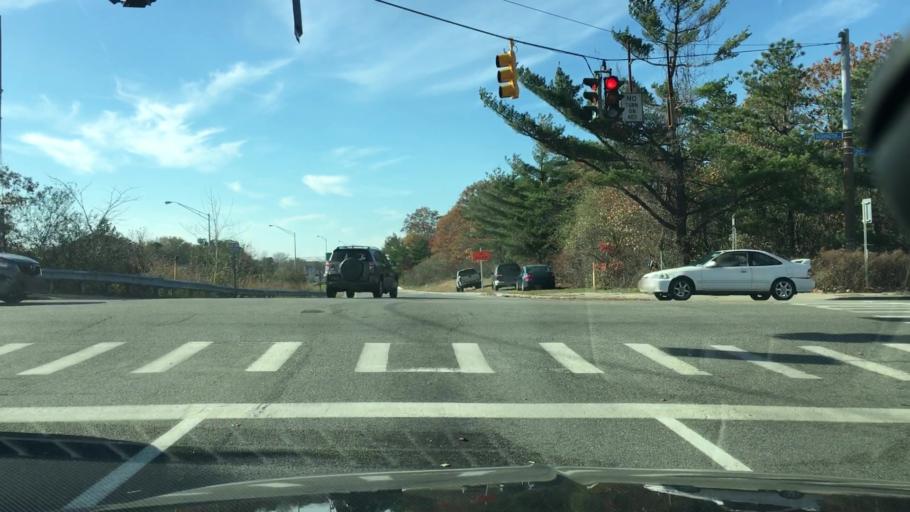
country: US
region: New York
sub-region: Suffolk County
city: Brentwood
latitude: 40.8061
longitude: -73.2486
